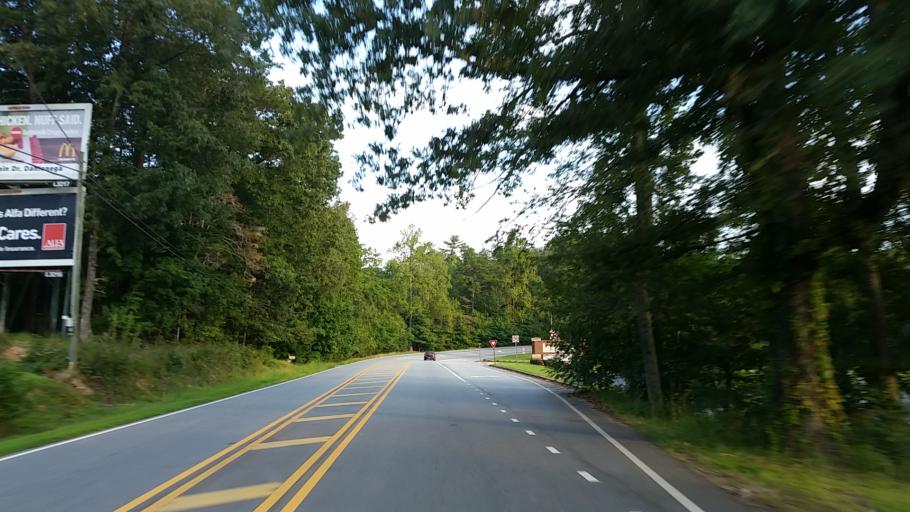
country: US
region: Georgia
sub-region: Lumpkin County
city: Dahlonega
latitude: 34.5557
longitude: -83.9963
